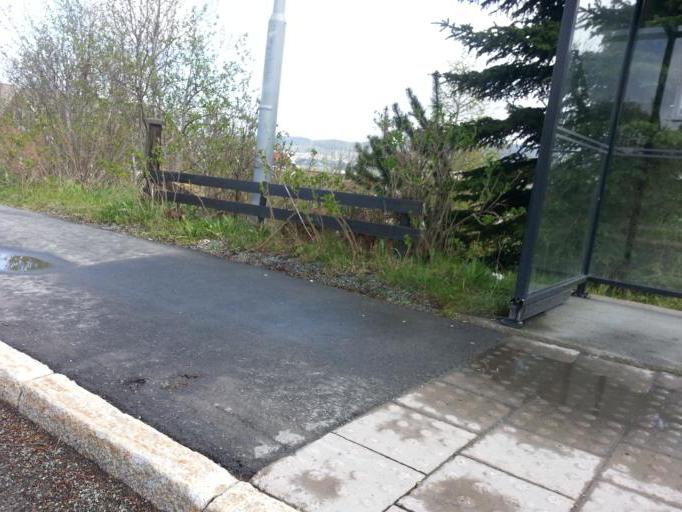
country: NO
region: Sor-Trondelag
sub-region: Trondheim
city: Trondheim
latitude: 63.3888
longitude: 10.3651
